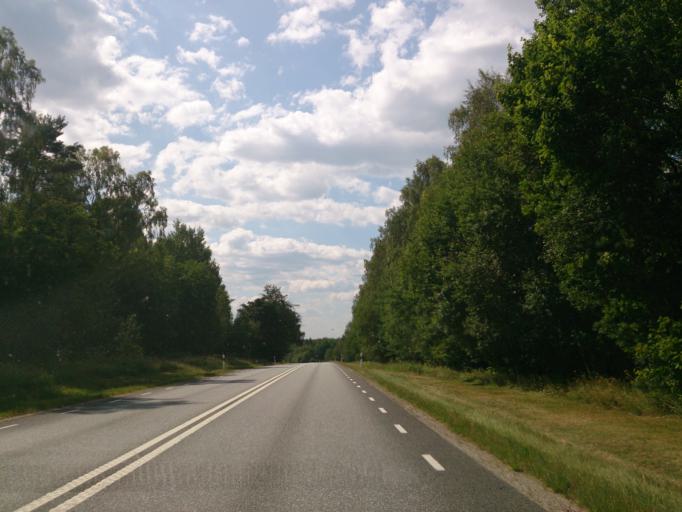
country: SE
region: Joenkoeping
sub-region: Varnamo Kommun
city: Bredaryd
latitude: 57.1738
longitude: 13.7217
